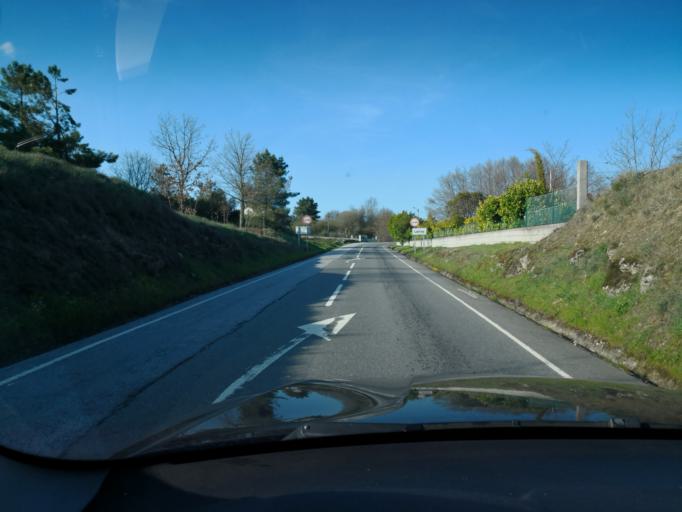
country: PT
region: Vila Real
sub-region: Vila Real
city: Vila Real
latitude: 41.3499
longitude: -7.6503
